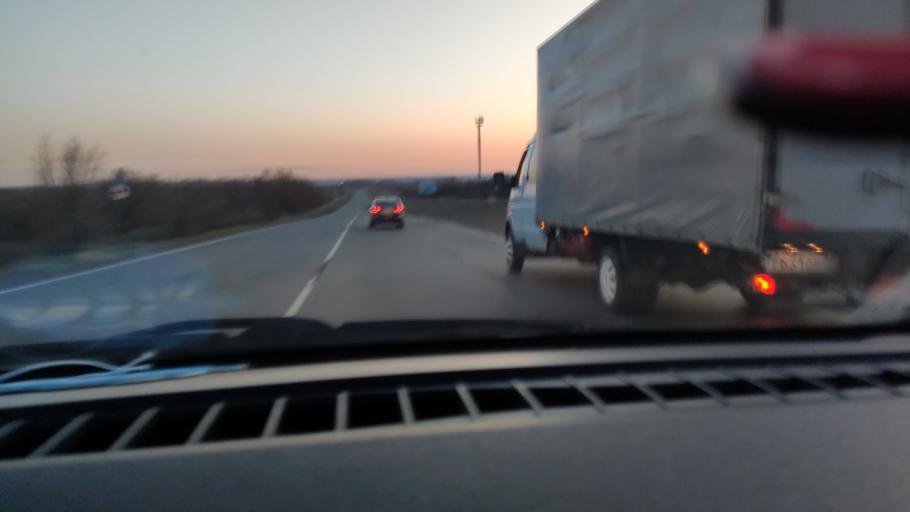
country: RU
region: Saratov
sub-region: Saratovskiy Rayon
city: Saratov
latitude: 51.6843
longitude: 46.0027
